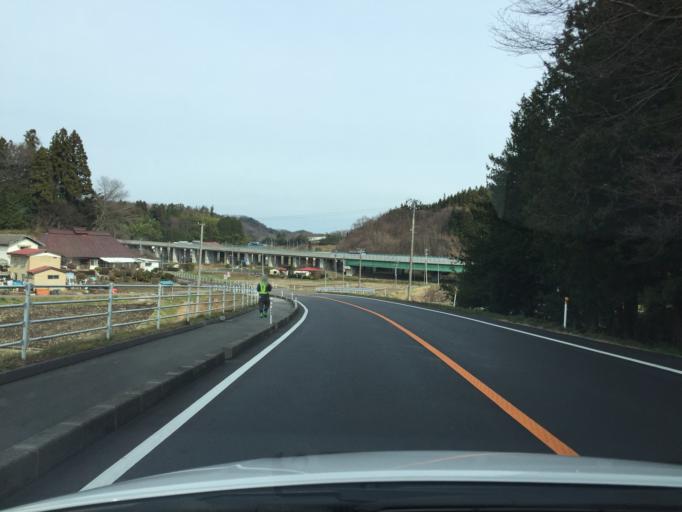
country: JP
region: Fukushima
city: Funehikimachi-funehiki
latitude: 37.3600
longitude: 140.6060
